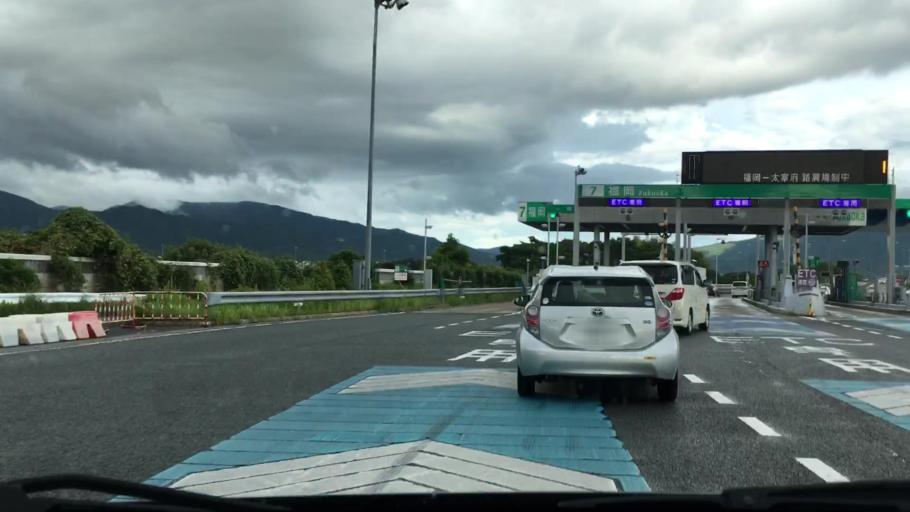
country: JP
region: Fukuoka
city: Sasaguri
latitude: 33.6306
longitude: 130.4862
